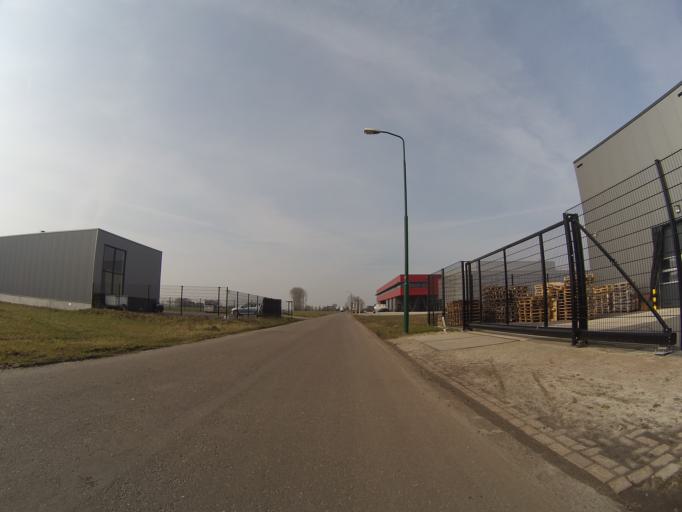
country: NL
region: Utrecht
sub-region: Gemeente Bunschoten
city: Bunschoten
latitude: 52.2240
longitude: 5.3751
